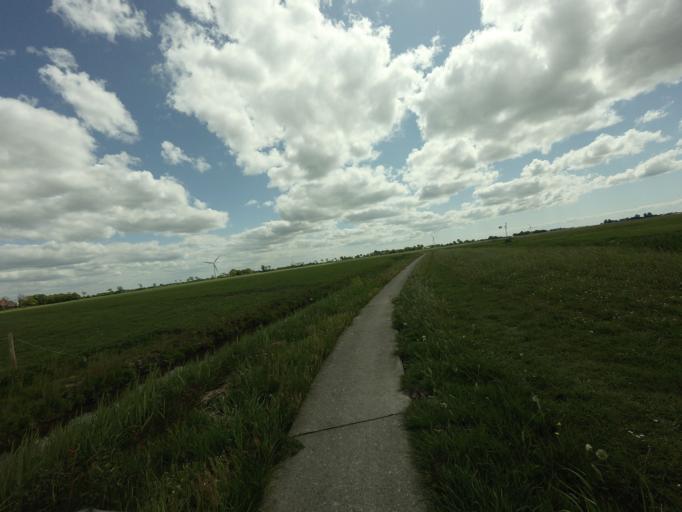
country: NL
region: Friesland
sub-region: Gemeente Littenseradiel
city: Wommels
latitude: 53.1322
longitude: 5.5736
